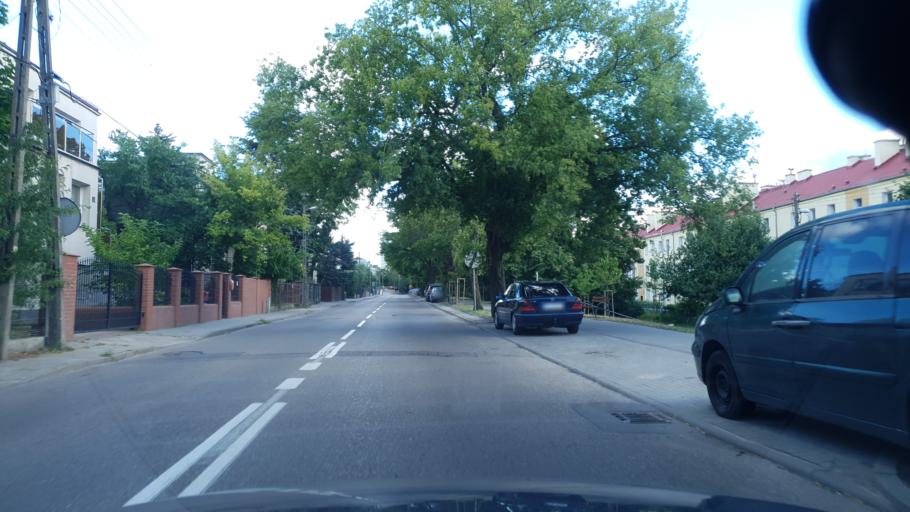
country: PL
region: Pomeranian Voivodeship
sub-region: Gdynia
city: Gdynia
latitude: 54.5014
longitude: 18.5411
